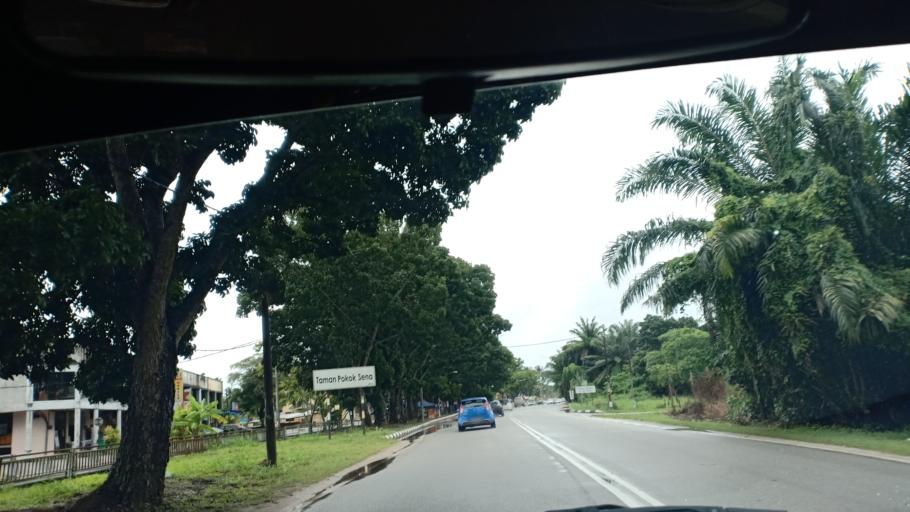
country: MY
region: Penang
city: Kepala Batas
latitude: 5.4933
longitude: 100.4527
